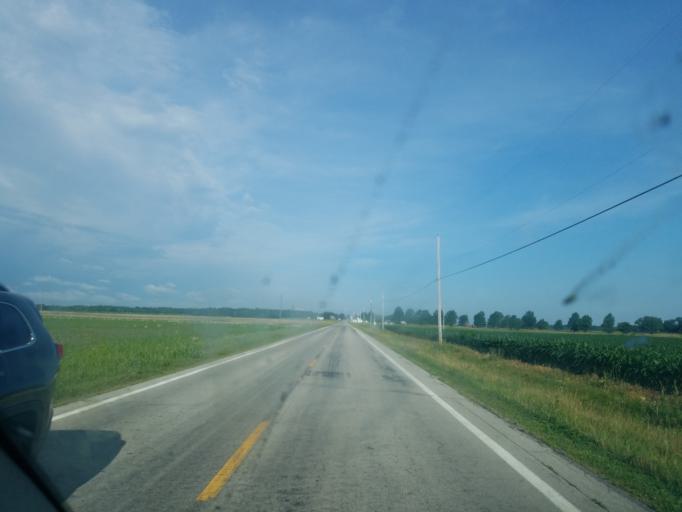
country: US
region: Ohio
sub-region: Wyandot County
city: Upper Sandusky
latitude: 40.7385
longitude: -83.2246
